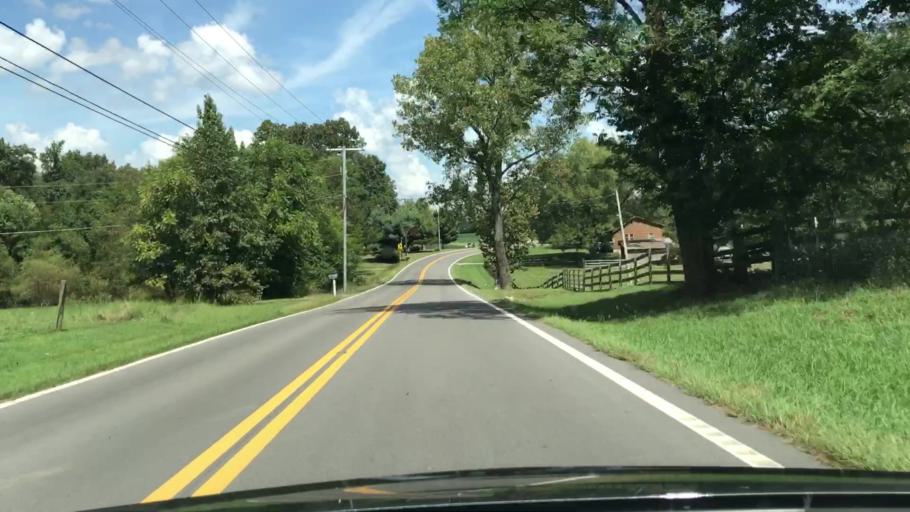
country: US
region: Tennessee
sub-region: Sumner County
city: Portland
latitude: 36.5417
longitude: -86.5224
